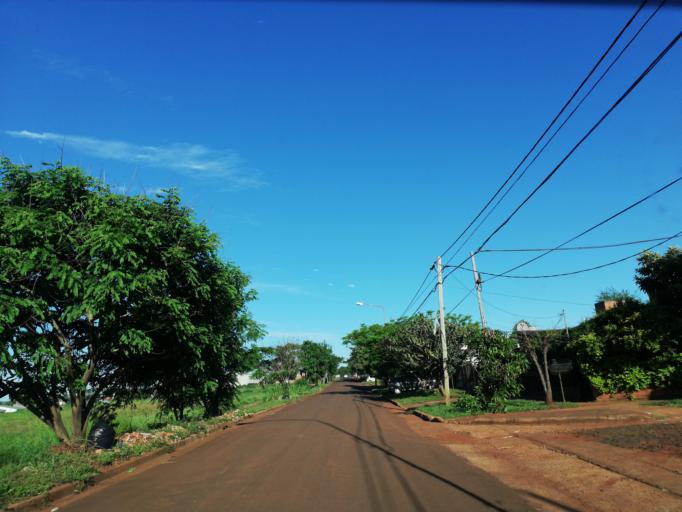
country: AR
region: Misiones
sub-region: Departamento de Capital
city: Posadas
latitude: -27.4356
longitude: -55.9185
